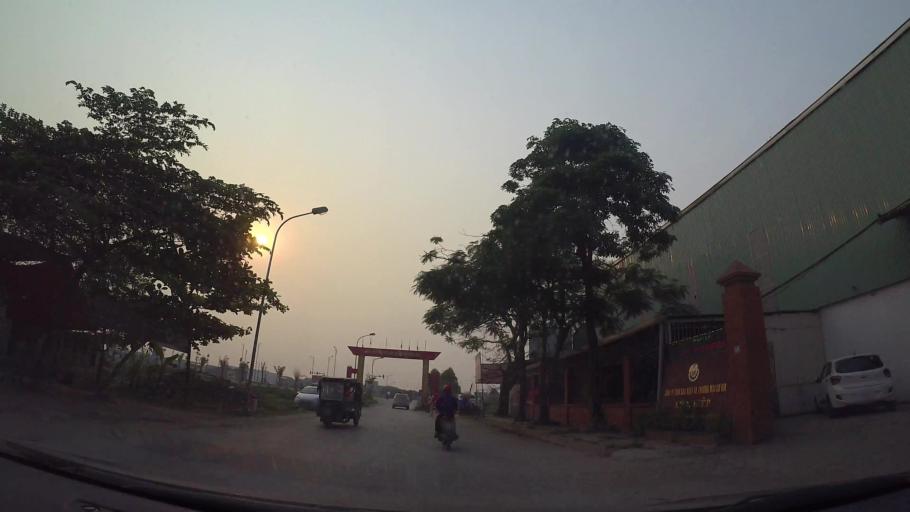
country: VN
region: Ha Noi
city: Kim Bai
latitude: 20.8718
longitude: 105.8046
